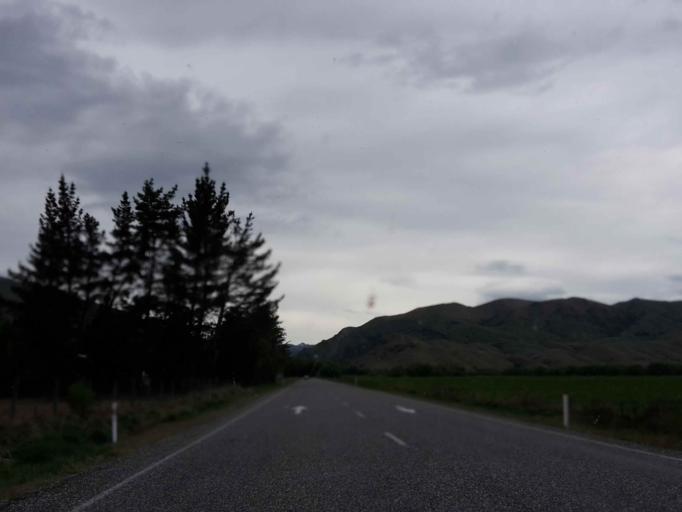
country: NZ
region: Otago
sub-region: Queenstown-Lakes District
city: Wanaka
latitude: -44.7730
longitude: 169.5088
